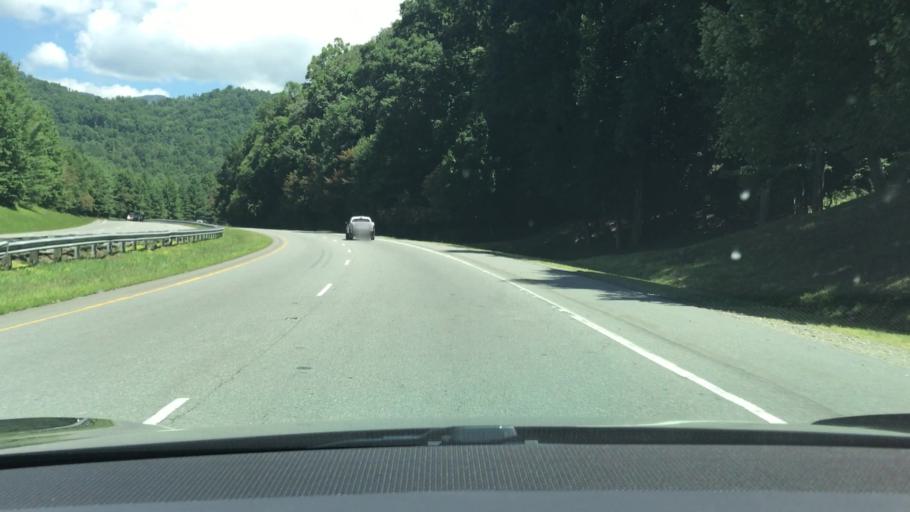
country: US
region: North Carolina
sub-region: Jackson County
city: Cullowhee
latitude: 35.3999
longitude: -83.1245
